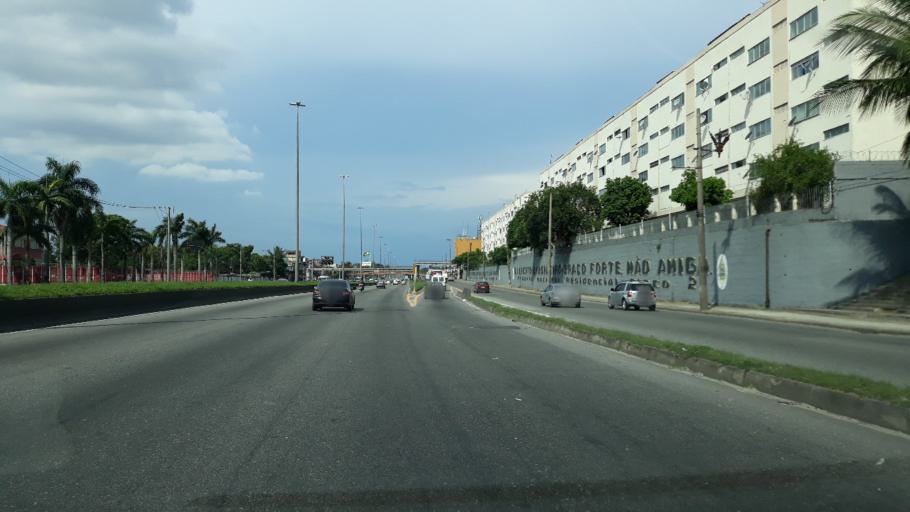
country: BR
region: Rio de Janeiro
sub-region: Sao Joao De Meriti
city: Sao Joao de Meriti
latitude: -22.8481
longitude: -43.3820
